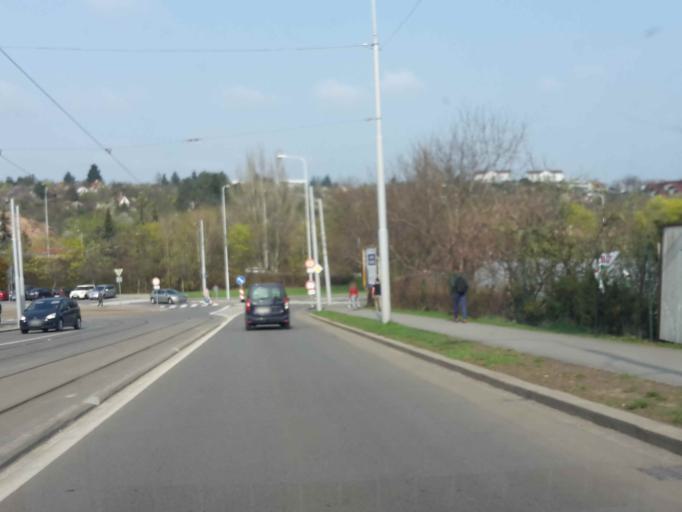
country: CZ
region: South Moravian
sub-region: Mesto Brno
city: Mokra Hora
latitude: 49.2289
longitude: 16.5951
